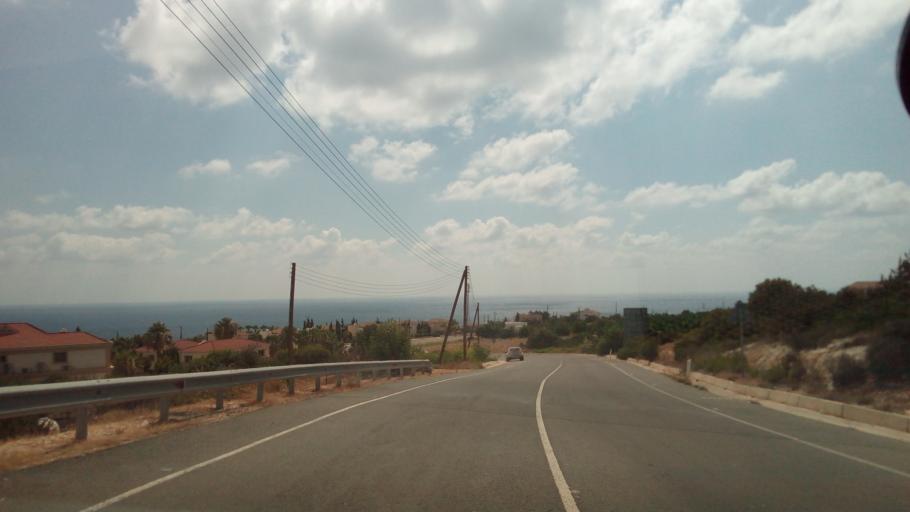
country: CY
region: Pafos
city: Pegeia
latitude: 34.8843
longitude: 32.3469
